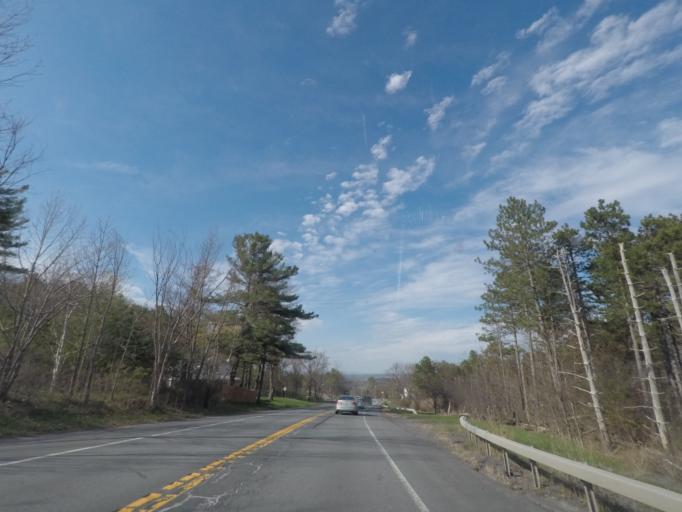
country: US
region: New York
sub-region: Albany County
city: Voorheesville
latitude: 42.6184
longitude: -73.9757
